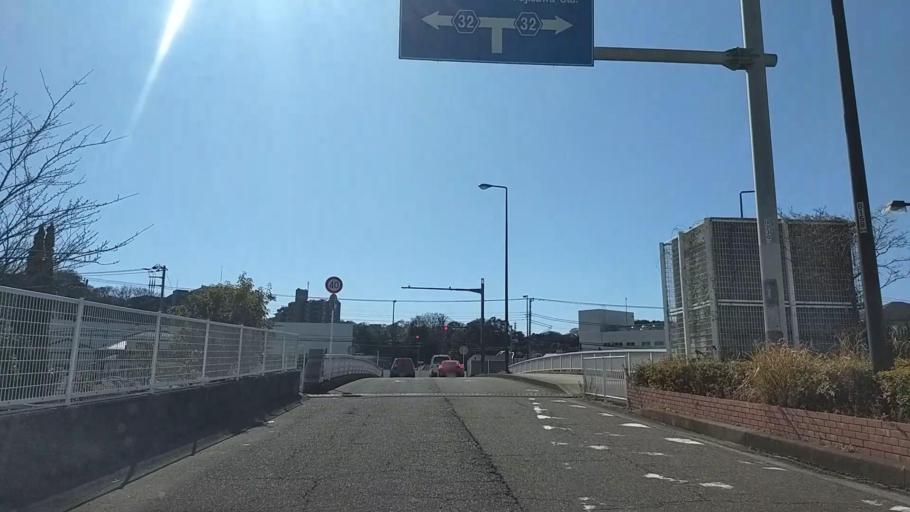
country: JP
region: Kanagawa
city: Fujisawa
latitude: 35.3333
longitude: 139.5006
